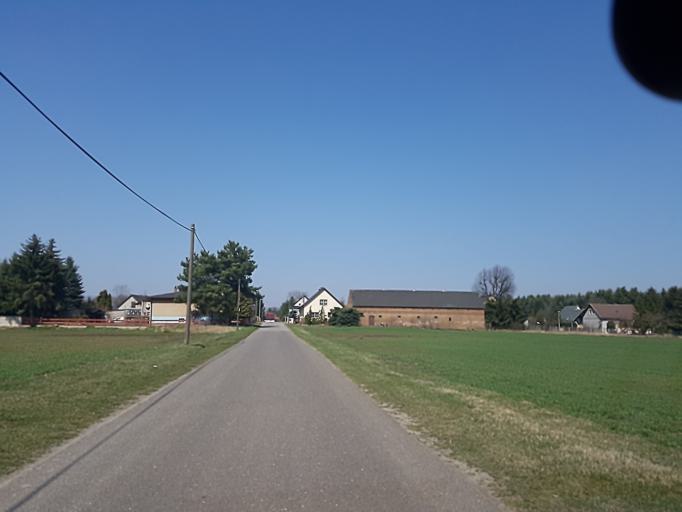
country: DE
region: Brandenburg
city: Tschernitz
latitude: 51.6496
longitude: 14.5798
